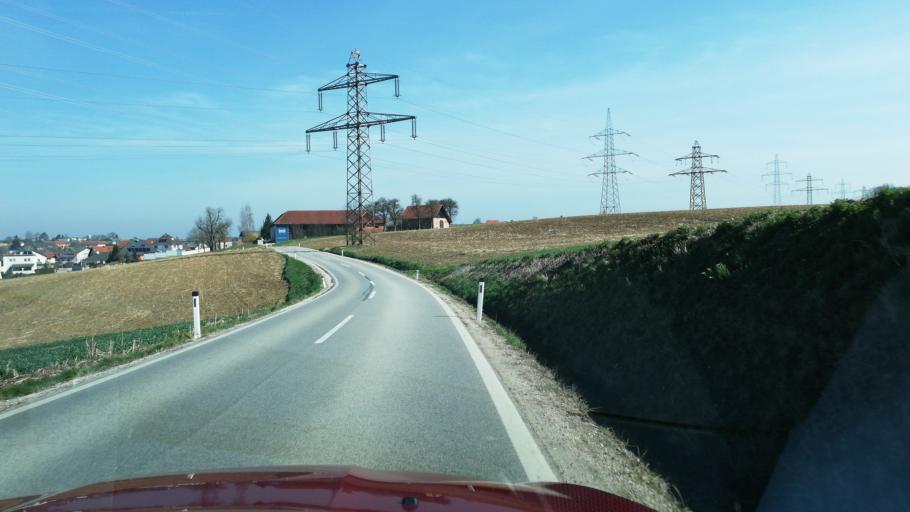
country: AT
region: Upper Austria
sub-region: Politischer Bezirk Kirchdorf an der Krems
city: Kremsmunster
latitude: 48.0909
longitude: 14.1106
